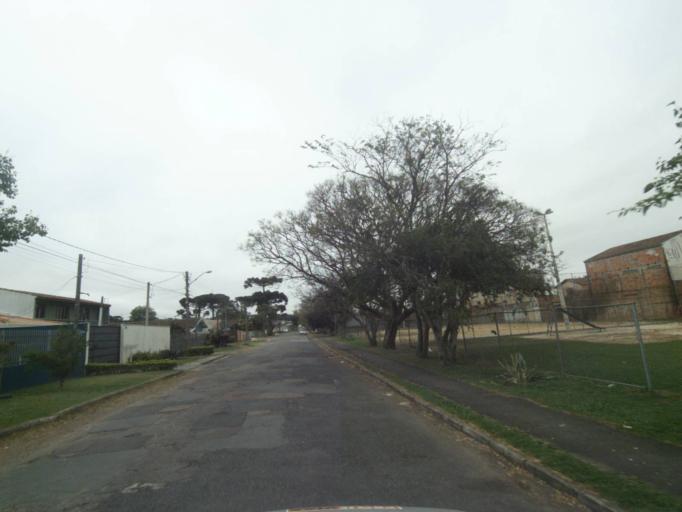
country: BR
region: Parana
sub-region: Sao Jose Dos Pinhais
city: Sao Jose dos Pinhais
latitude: -25.4990
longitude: -49.2126
